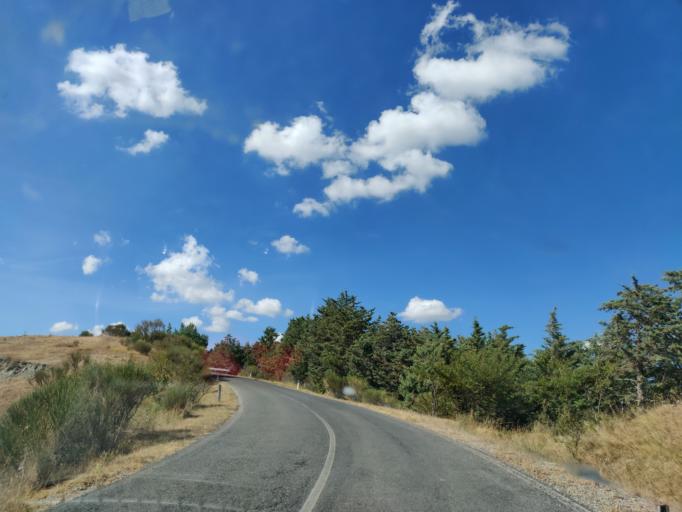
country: IT
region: Tuscany
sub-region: Provincia di Siena
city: Radicofani
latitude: 42.9456
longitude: 11.7348
